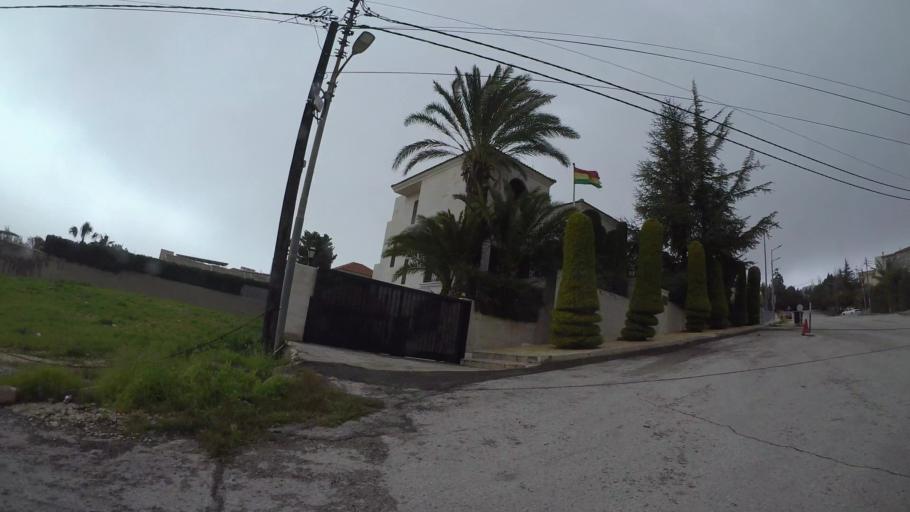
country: JO
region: Amman
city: Al Bunayyat ash Shamaliyah
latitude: 31.9337
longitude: 35.8801
